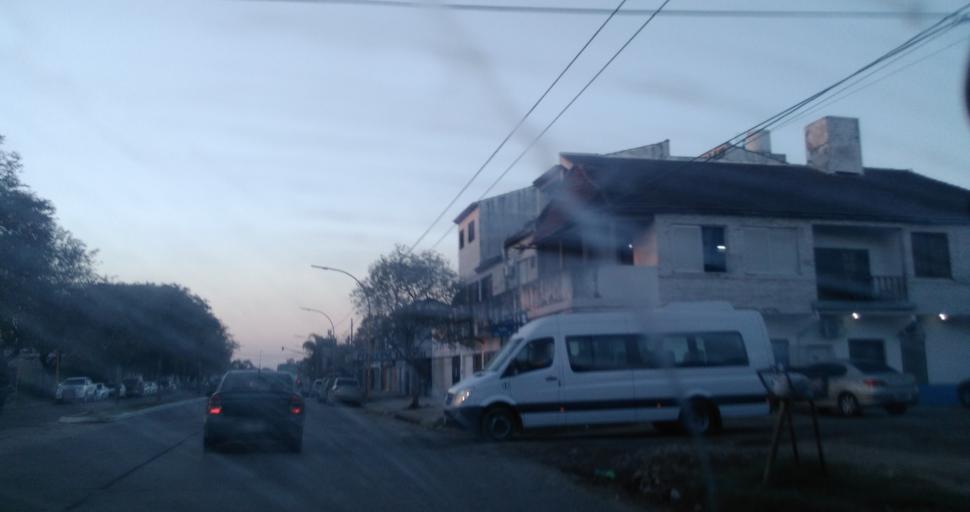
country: AR
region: Chaco
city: Resistencia
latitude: -27.4671
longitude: -58.9686
